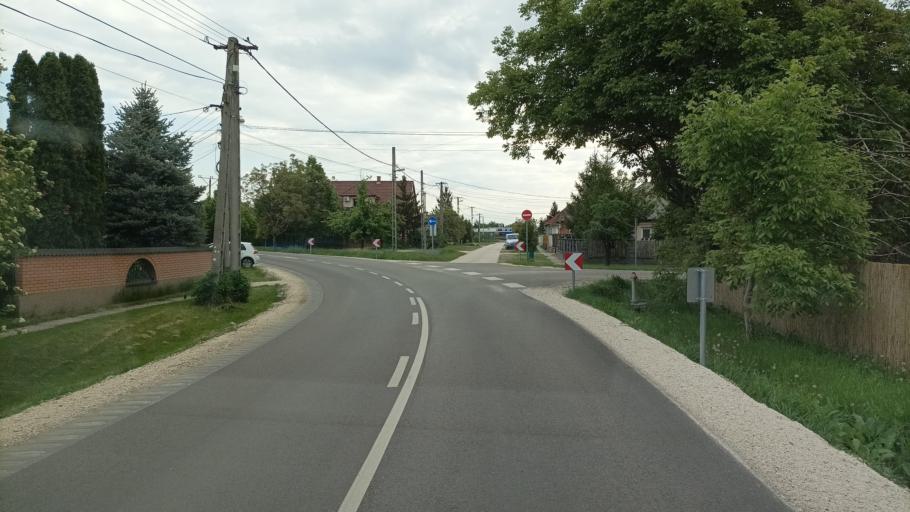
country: HU
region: Pest
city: Pilis
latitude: 47.2794
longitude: 19.5327
